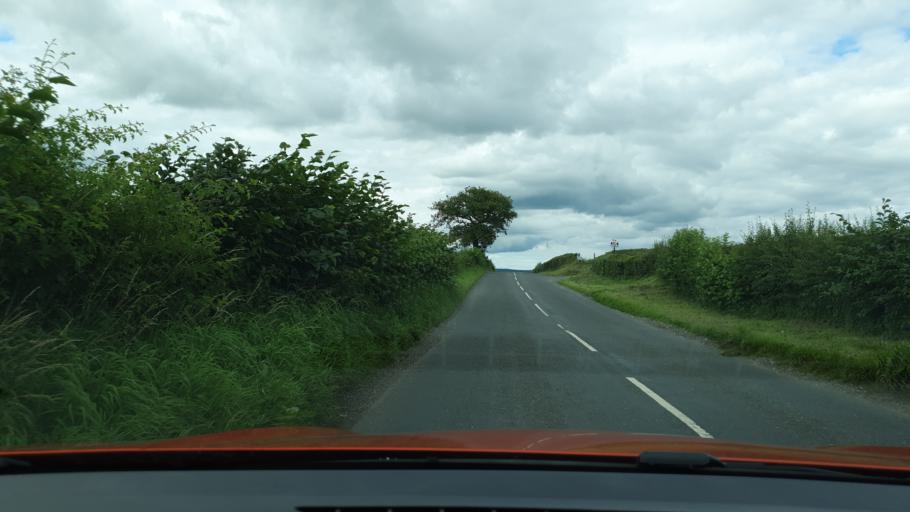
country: GB
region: England
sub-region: Cumbria
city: Penrith
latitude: 54.6228
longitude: -2.7978
